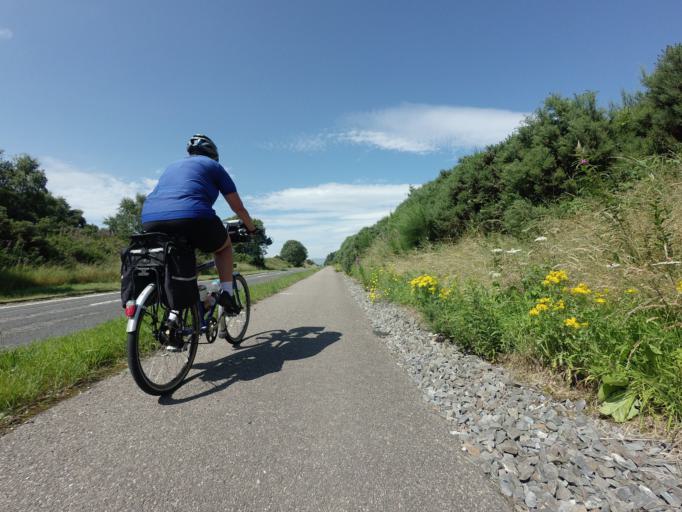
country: GB
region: Scotland
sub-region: Highland
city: Conon Bridge
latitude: 57.5437
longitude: -4.3803
